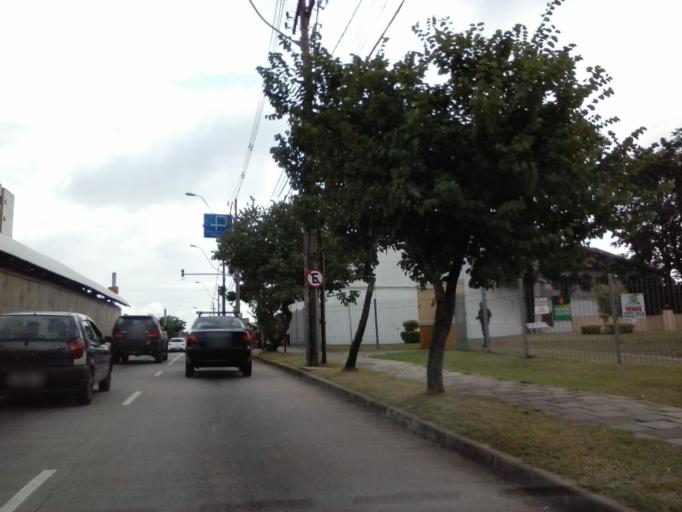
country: BR
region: Rio Grande do Sul
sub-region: Porto Alegre
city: Porto Alegre
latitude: -30.0720
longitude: -51.1923
